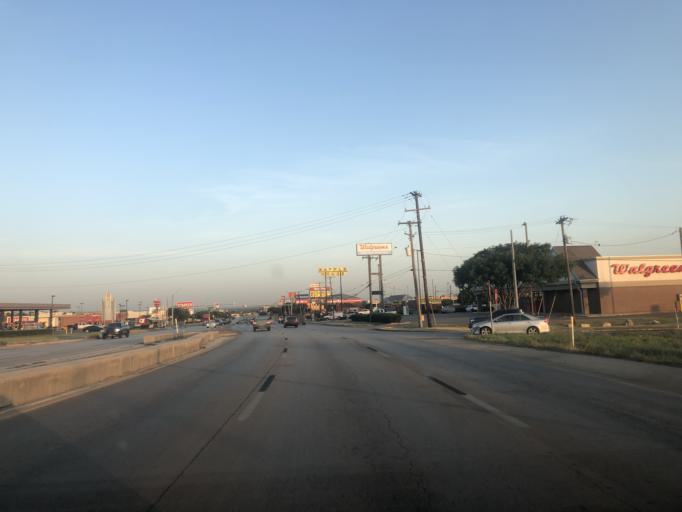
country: US
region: Texas
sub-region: Tarrant County
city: Sansom Park
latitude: 32.8096
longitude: -97.4198
